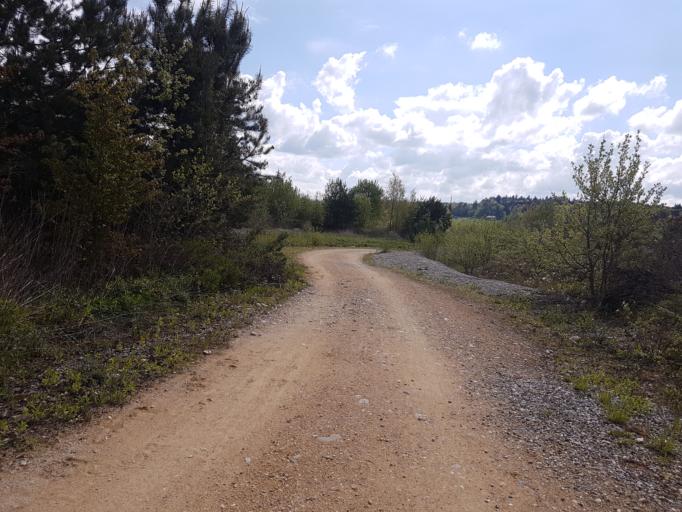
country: CH
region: Solothurn
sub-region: Bezirk Olten
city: Gunzgen
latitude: 47.2968
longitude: 7.8460
